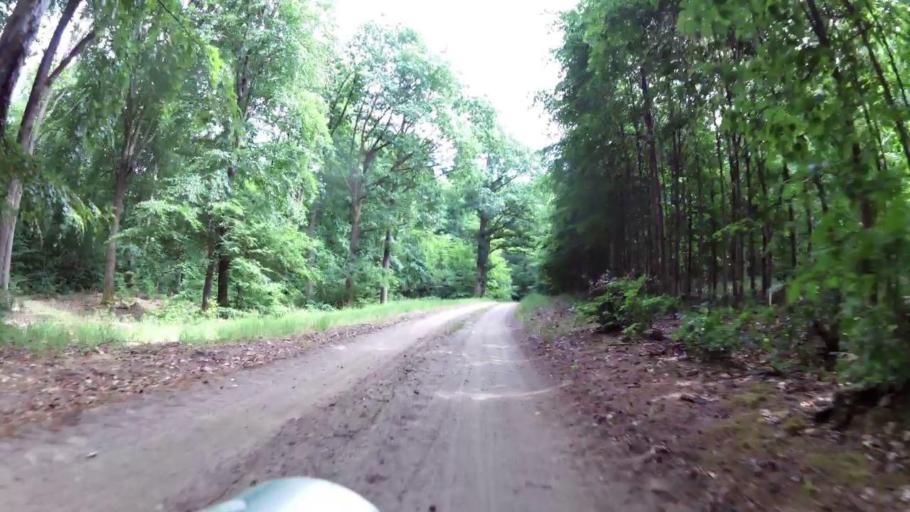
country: PL
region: West Pomeranian Voivodeship
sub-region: Powiat koszalinski
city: Bobolice
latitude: 53.9539
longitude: 16.6794
